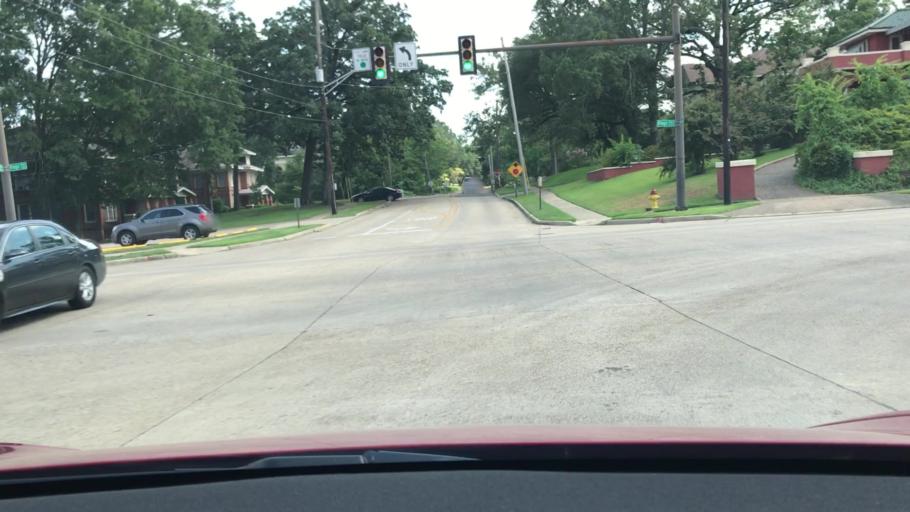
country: US
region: Louisiana
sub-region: Bossier Parish
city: Bossier City
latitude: 32.4819
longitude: -93.7339
